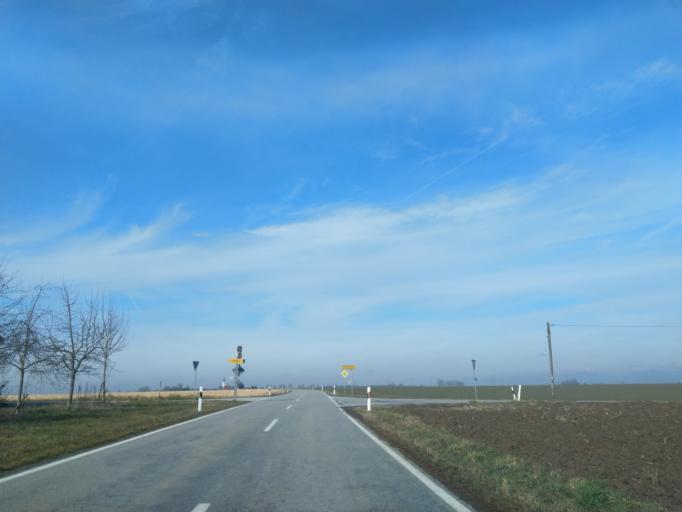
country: DE
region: Bavaria
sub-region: Lower Bavaria
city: Buchhofen
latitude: 48.6783
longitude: 12.9616
